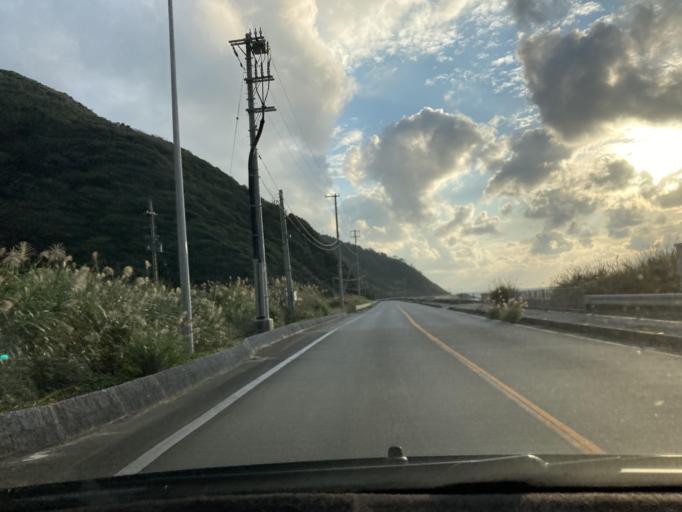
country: JP
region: Okinawa
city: Nago
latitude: 26.8259
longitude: 128.2449
